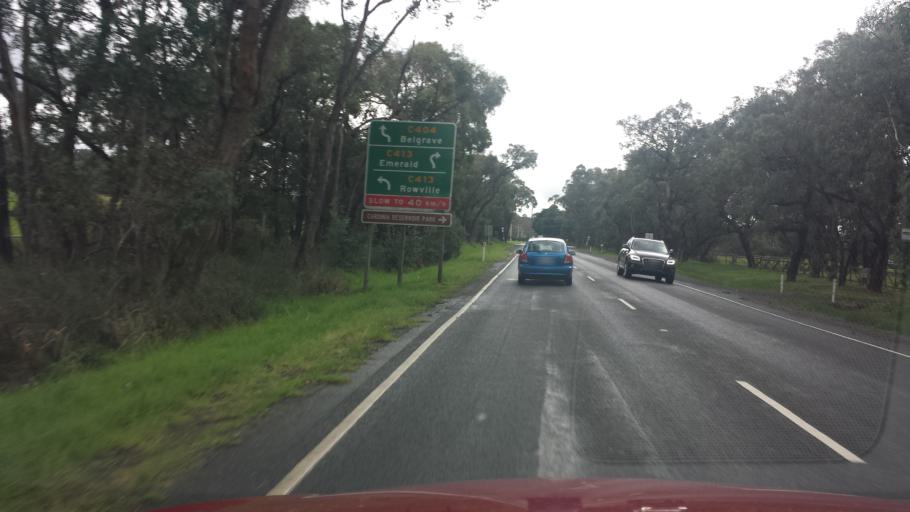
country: AU
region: Victoria
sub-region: Yarra Ranges
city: Belgrave South
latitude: -37.9565
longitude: 145.3465
